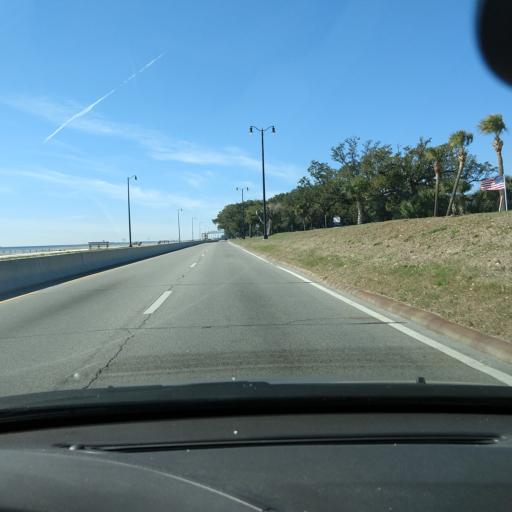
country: US
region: Mississippi
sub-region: Harrison County
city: Gulfport
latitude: 30.3862
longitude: -89.0101
